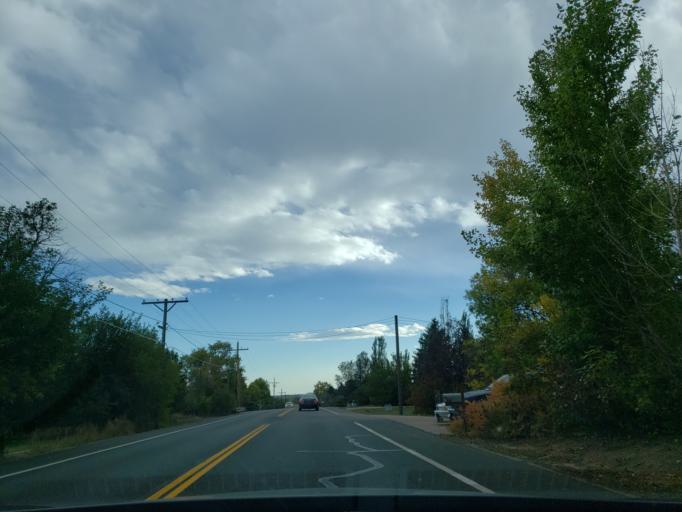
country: US
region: Colorado
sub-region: Larimer County
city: Fort Collins
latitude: 40.6142
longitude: -105.0387
